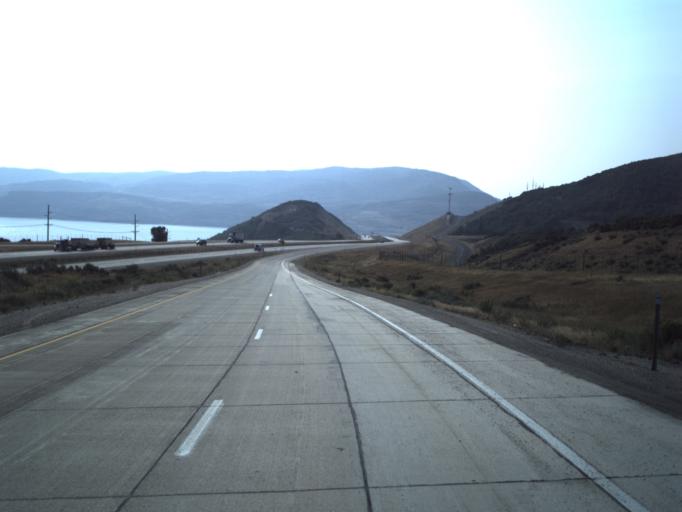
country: US
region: Utah
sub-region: Summit County
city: Park City
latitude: 40.6242
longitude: -111.4410
